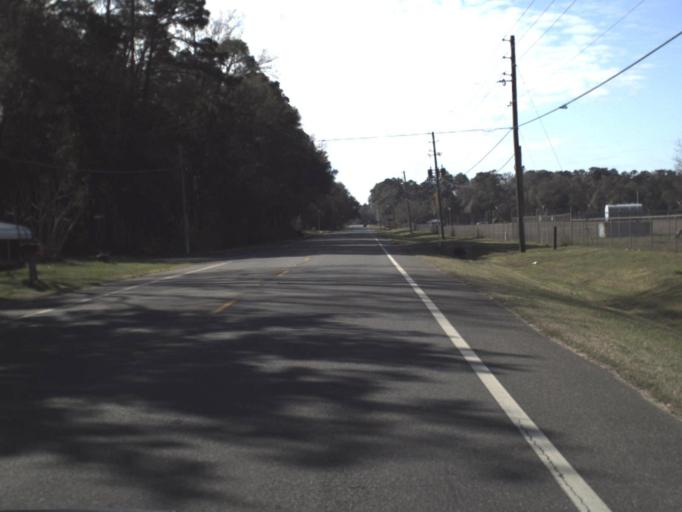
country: US
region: Florida
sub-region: Jackson County
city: Marianna
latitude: 30.8365
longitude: -85.1666
